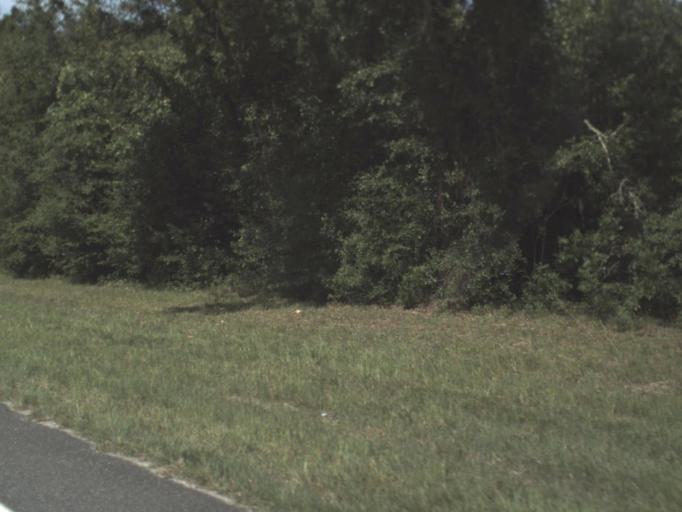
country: US
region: Florida
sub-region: Alachua County
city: High Springs
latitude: 29.8801
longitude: -82.7344
